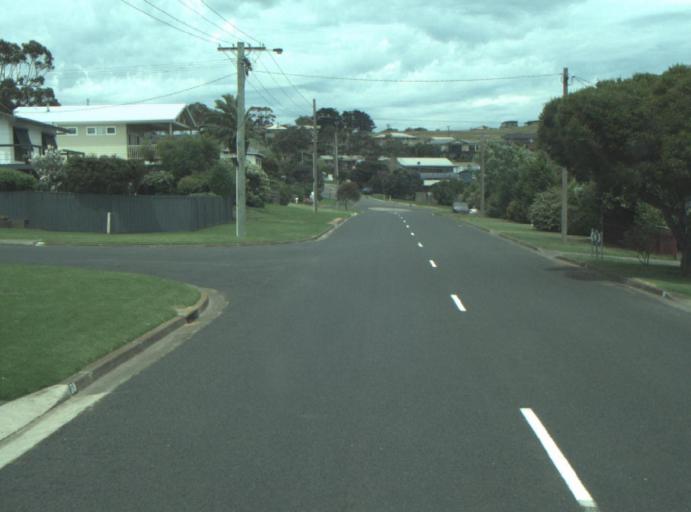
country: AU
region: Victoria
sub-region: Greater Geelong
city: Clifton Springs
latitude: -38.1185
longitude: 144.6454
